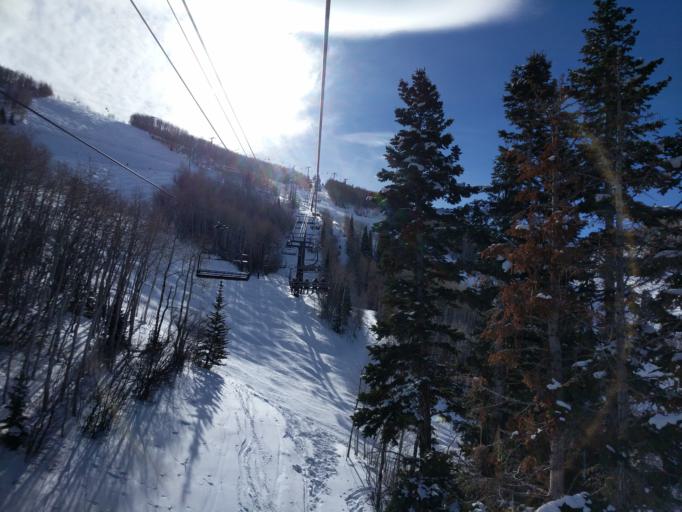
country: US
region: Utah
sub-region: Summit County
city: Park City
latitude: 40.6406
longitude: -111.5081
